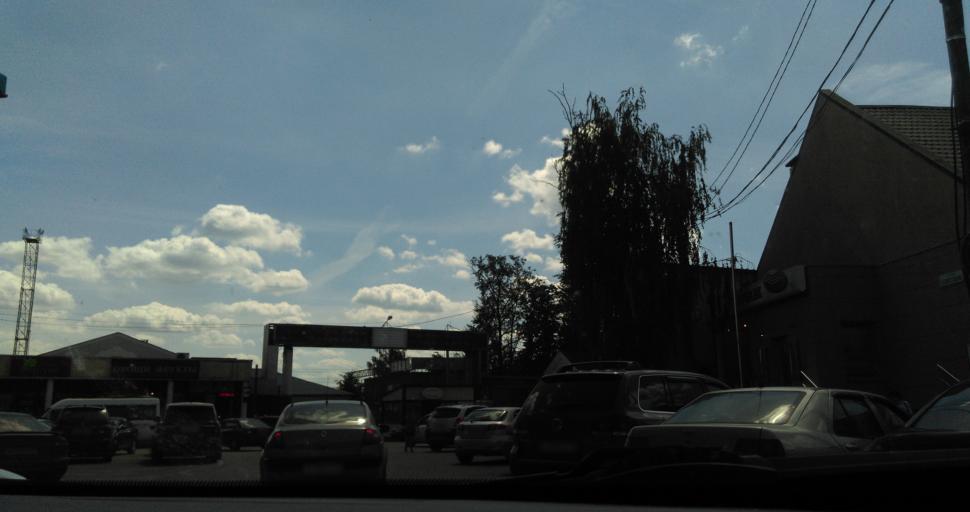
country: RU
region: Moskovskaya
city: Tuchkovo
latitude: 55.5984
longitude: 36.4678
